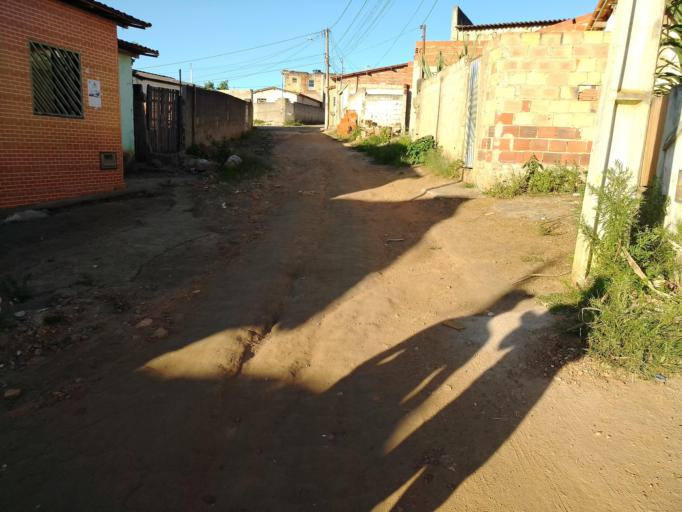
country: BR
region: Bahia
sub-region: Pocoes
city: Pocoes
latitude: -14.7510
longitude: -40.5115
